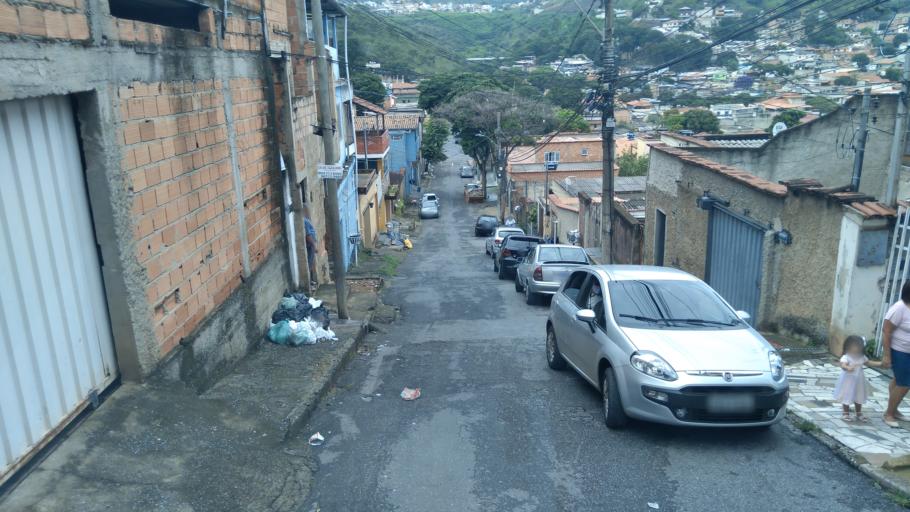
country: BR
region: Minas Gerais
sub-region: Belo Horizonte
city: Belo Horizonte
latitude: -19.9141
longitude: -43.8913
